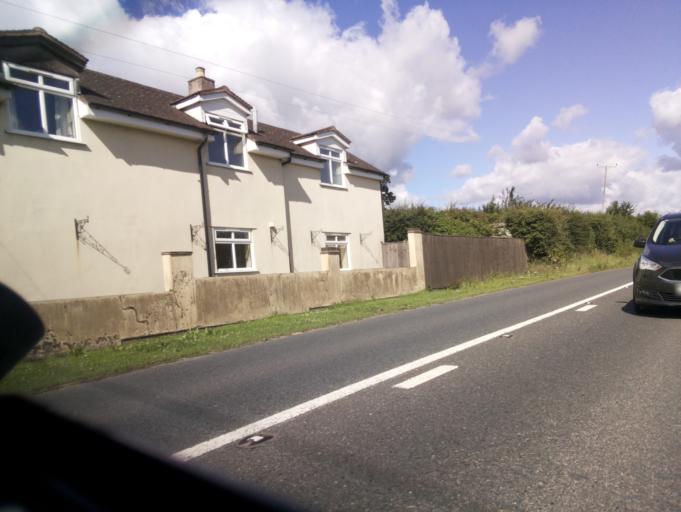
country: GB
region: England
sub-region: Gloucestershire
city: Gloucester
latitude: 51.8883
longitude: -2.3180
